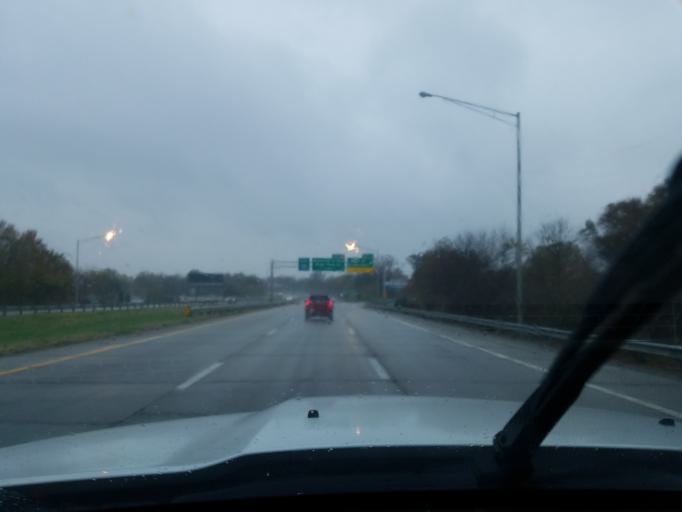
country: US
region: Indiana
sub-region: Floyd County
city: New Albany
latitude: 38.2718
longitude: -85.8087
